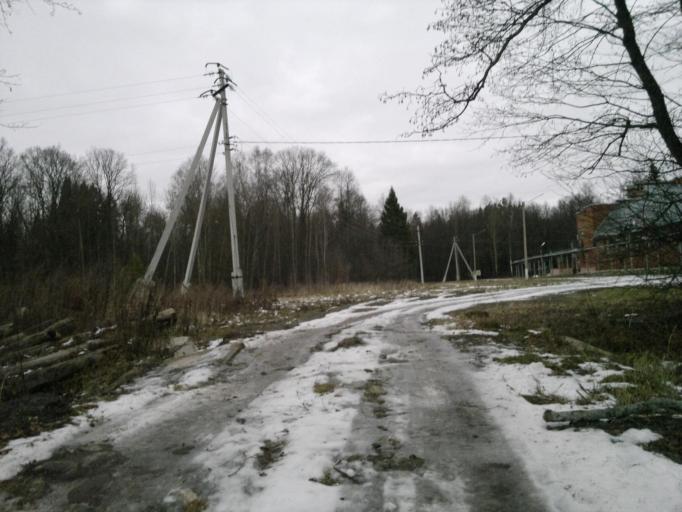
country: RU
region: Mariy-El
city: Yoshkar-Ola
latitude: 56.5974
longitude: 47.9697
